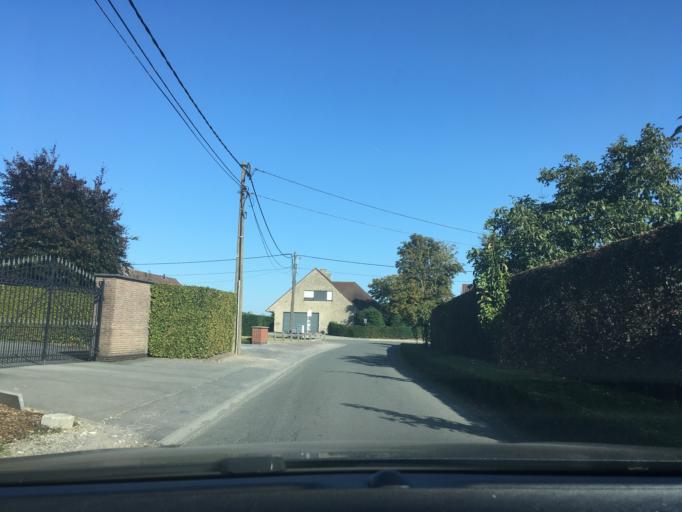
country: BE
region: Flanders
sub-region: Provincie West-Vlaanderen
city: Ledegem
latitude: 50.8800
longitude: 3.1586
